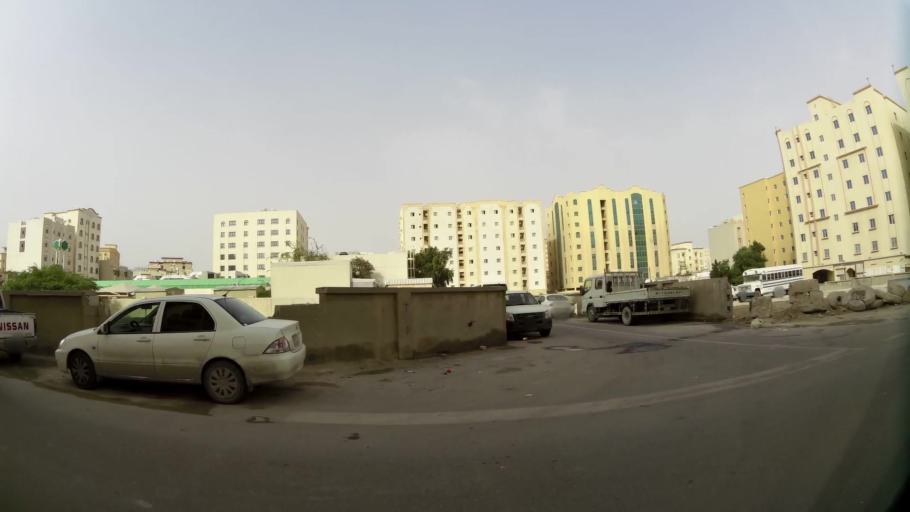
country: QA
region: Baladiyat ad Dawhah
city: Doha
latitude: 25.2777
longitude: 51.5460
